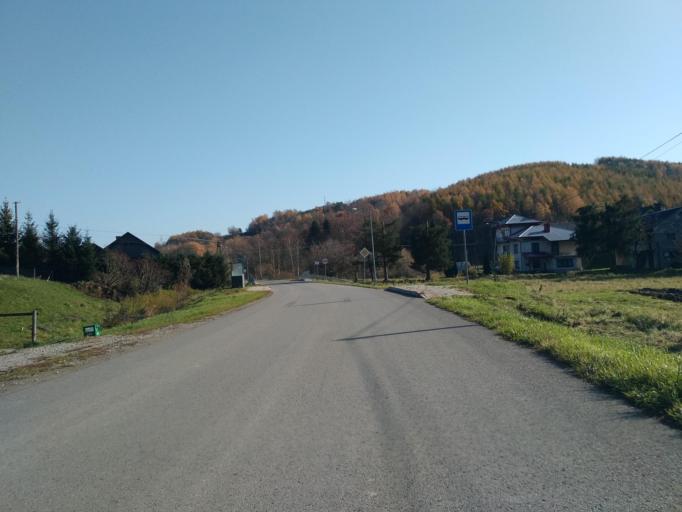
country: PL
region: Subcarpathian Voivodeship
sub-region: Powiat brzozowski
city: Nozdrzec
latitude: 49.7922
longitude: 22.1861
